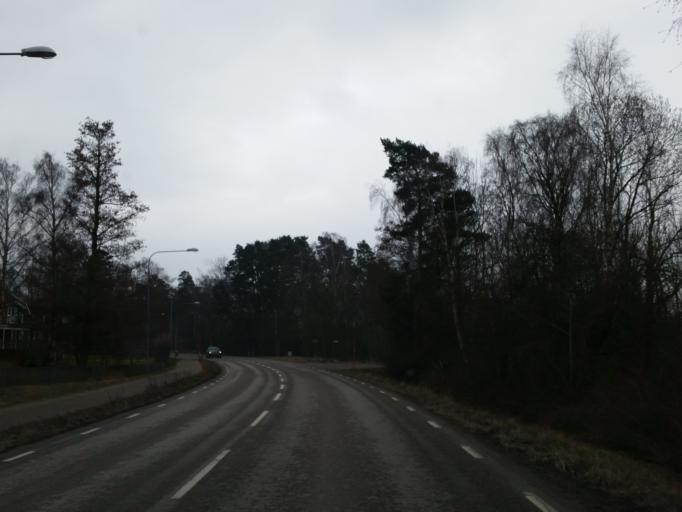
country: SE
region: Kalmar
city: Faerjestaden
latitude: 56.6396
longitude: 16.4636
